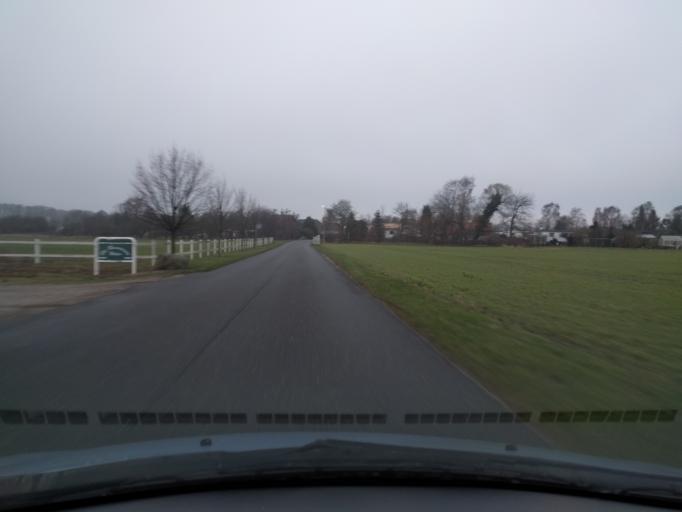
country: DK
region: South Denmark
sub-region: Odense Kommune
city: Bullerup
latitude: 55.4032
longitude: 10.5108
